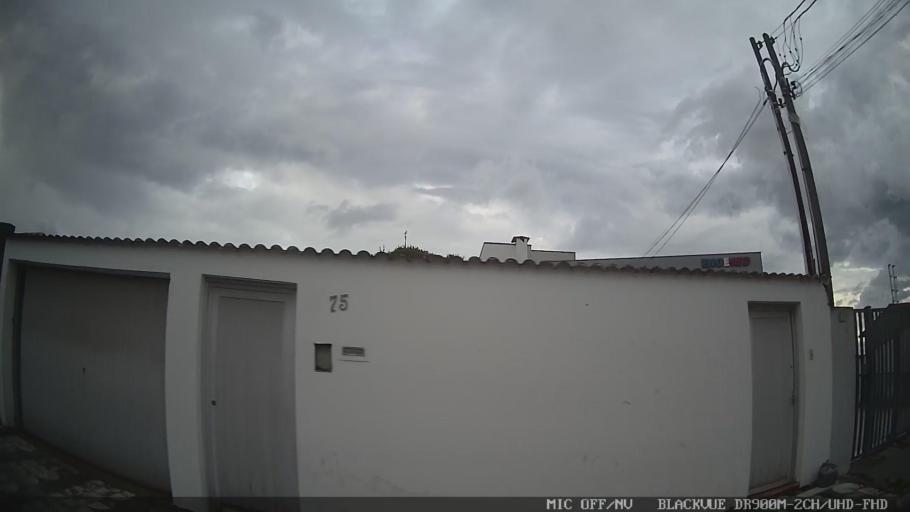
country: BR
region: Sao Paulo
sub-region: Mogi das Cruzes
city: Mogi das Cruzes
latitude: -23.5332
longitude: -46.1977
